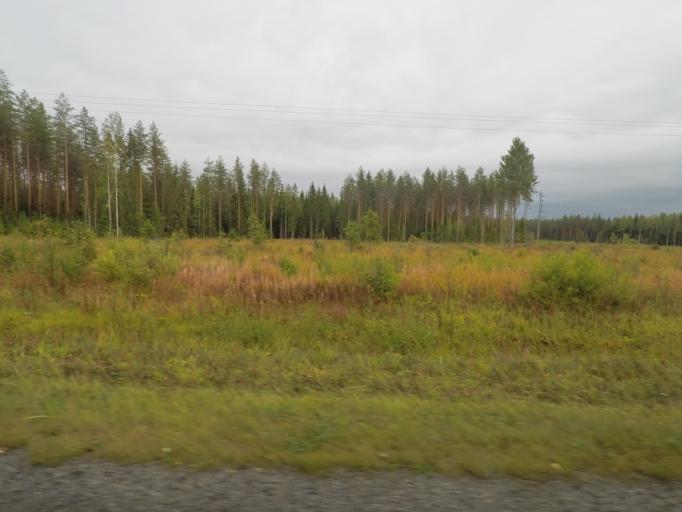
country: FI
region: Southern Savonia
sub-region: Pieksaemaeki
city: Juva
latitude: 61.9686
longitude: 27.8043
